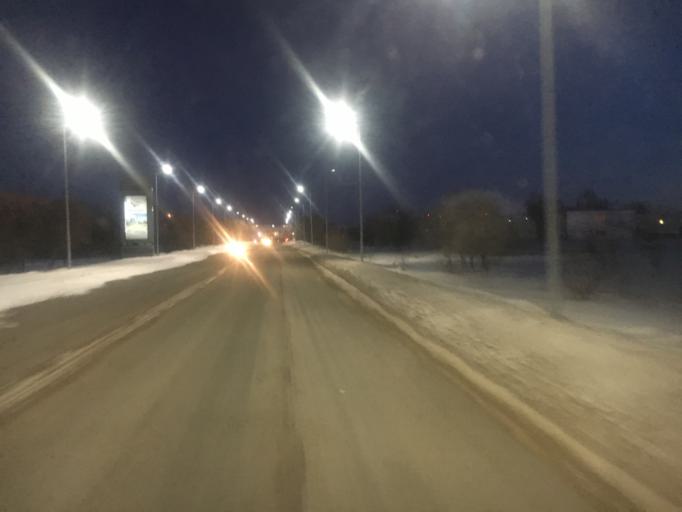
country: KZ
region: Batys Qazaqstan
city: Oral
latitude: 51.1566
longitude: 51.5346
